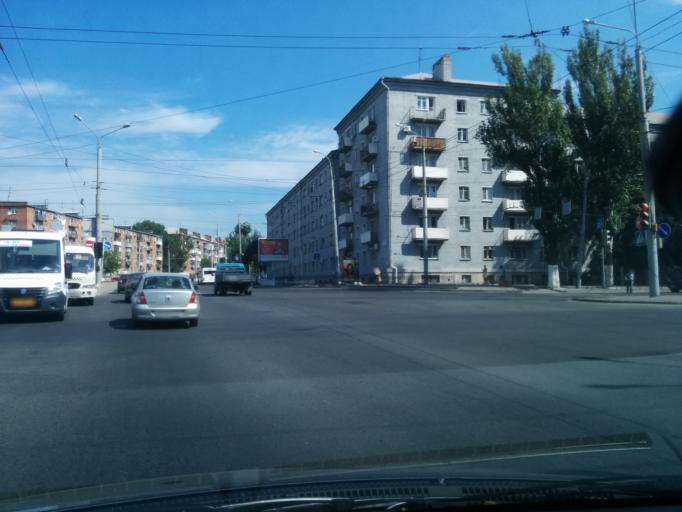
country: RU
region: Rostov
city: Rostov-na-Donu
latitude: 47.2493
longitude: 39.7128
